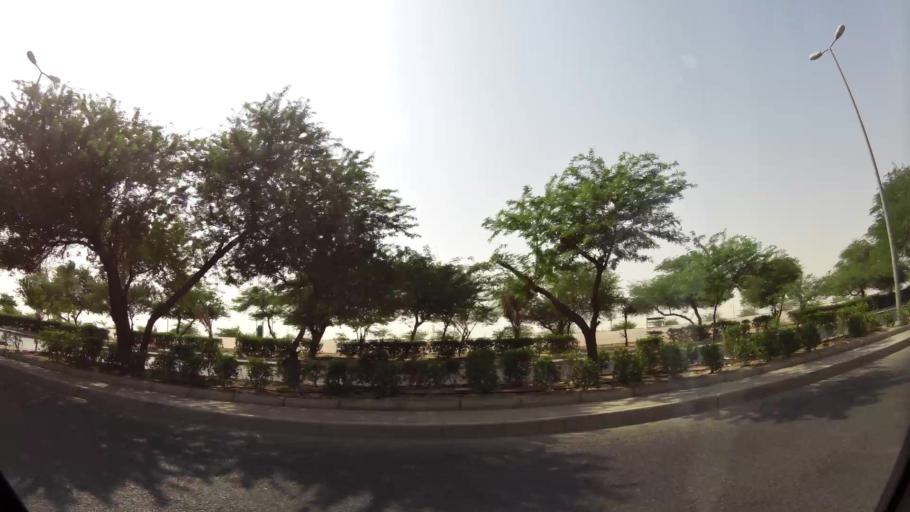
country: KW
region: Muhafazat al Jahra'
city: Al Jahra'
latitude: 29.3264
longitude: 47.6475
